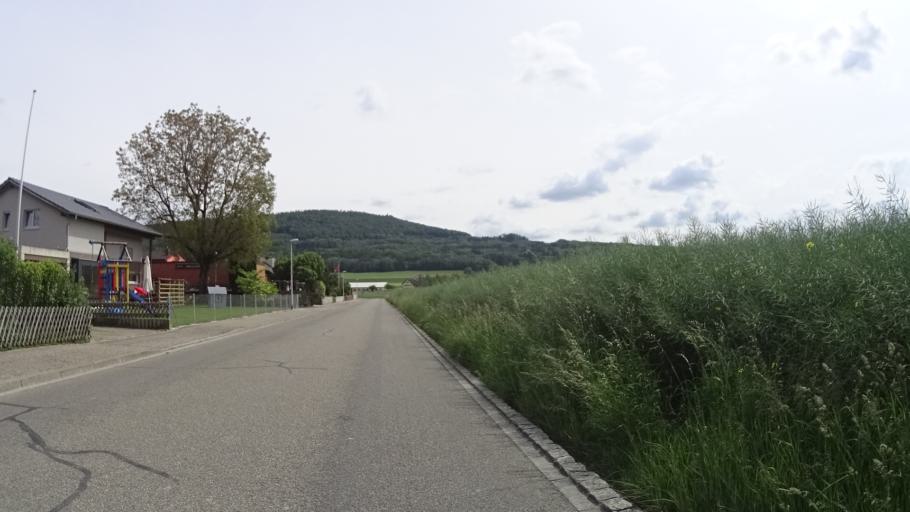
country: CH
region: Aargau
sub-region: Bezirk Rheinfelden
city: Mohlin
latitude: 47.5528
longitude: 7.8425
